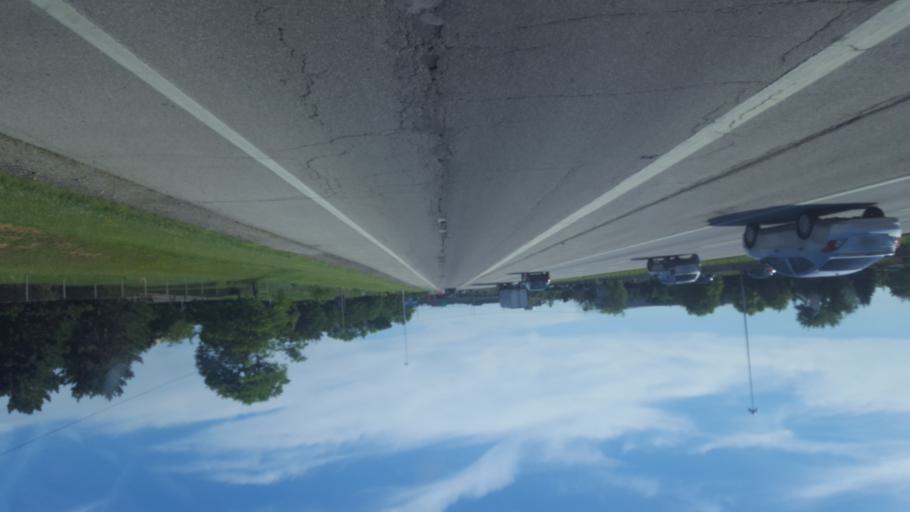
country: US
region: Ohio
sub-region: Franklin County
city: Dublin
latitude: 40.0791
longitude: -83.1362
